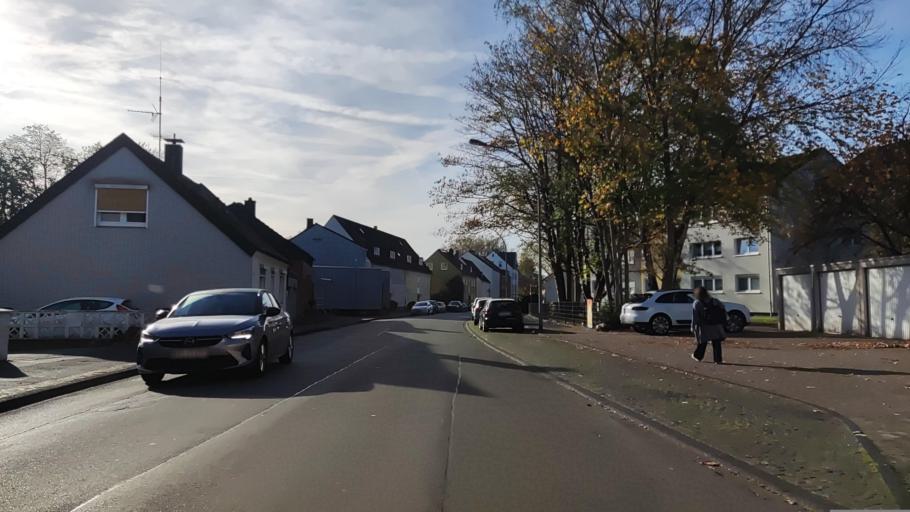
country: DE
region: North Rhine-Westphalia
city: Bochum-Hordel
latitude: 51.5244
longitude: 7.1831
